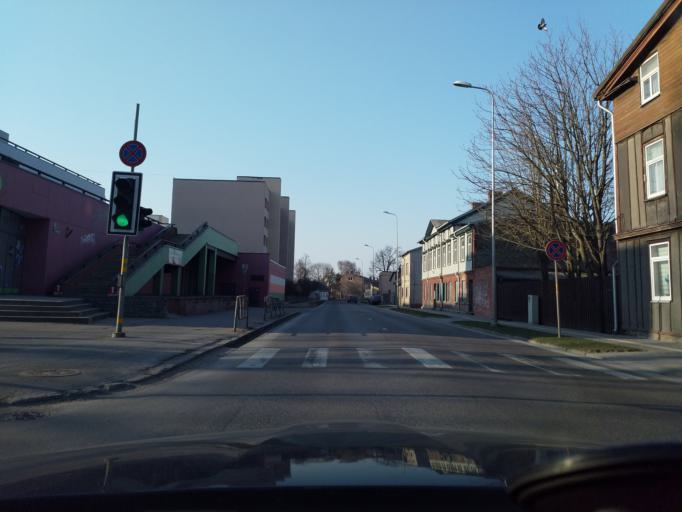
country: LV
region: Liepaja
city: Liepaja
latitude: 56.5028
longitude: 21.0188
